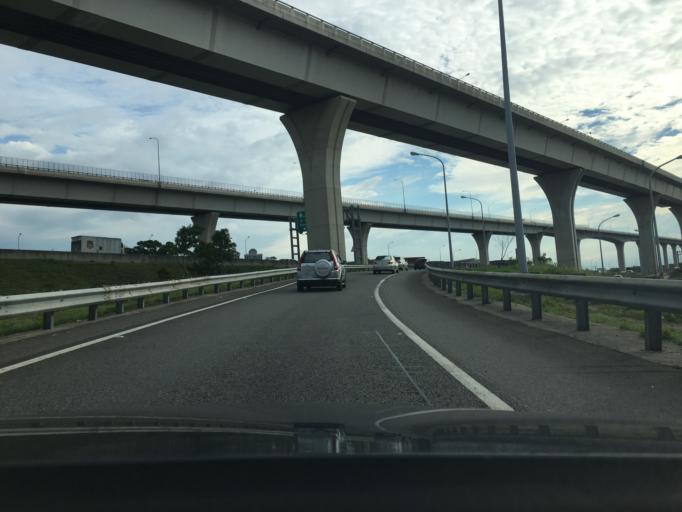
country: TW
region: Taiwan
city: Taoyuan City
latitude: 25.0383
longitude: 121.2967
